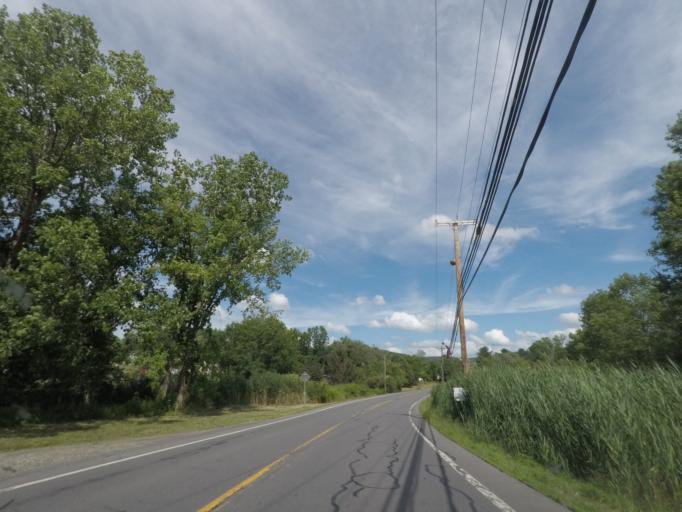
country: US
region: New York
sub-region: Rensselaer County
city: Poestenkill
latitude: 42.6965
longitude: -73.5834
